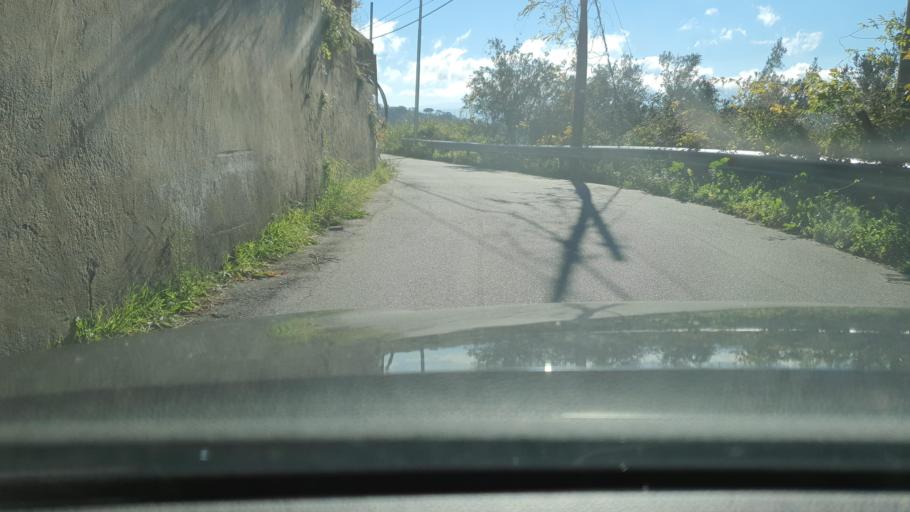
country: IT
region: Calabria
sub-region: Provincia di Catanzaro
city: Sant'Elia
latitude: 38.9536
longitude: 16.5808
